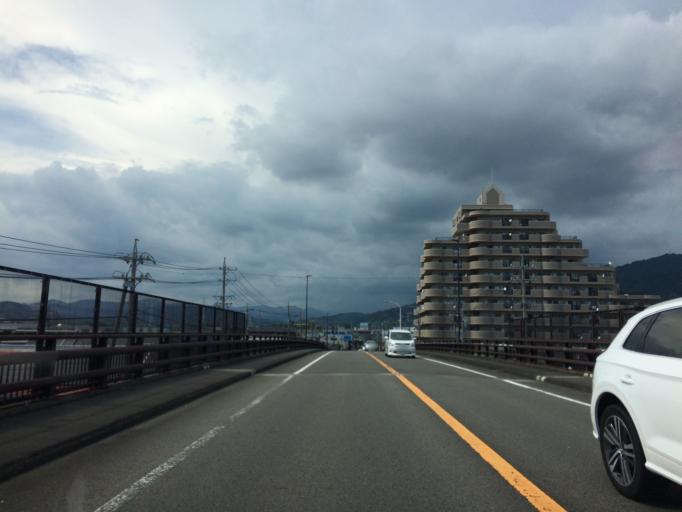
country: JP
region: Shizuoka
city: Yaizu
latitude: 34.8705
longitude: 138.3147
